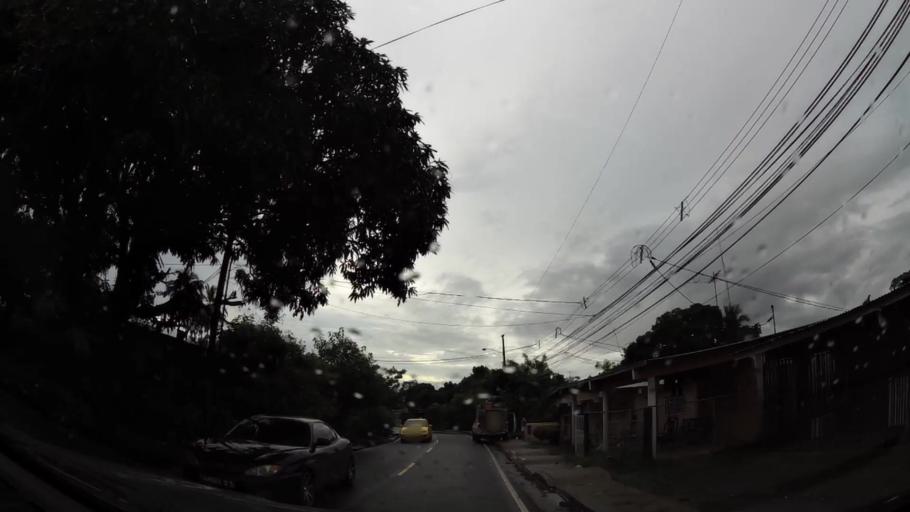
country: PA
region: Veraguas
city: Santiago de Veraguas
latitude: 8.1004
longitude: -80.9722
